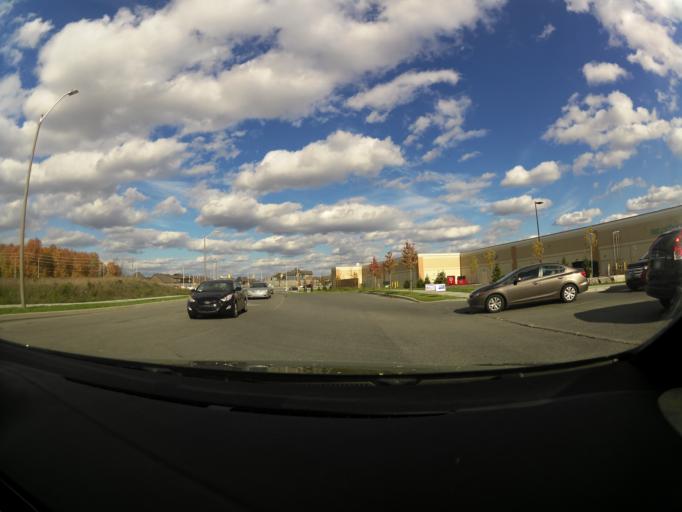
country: CA
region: Ontario
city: Bells Corners
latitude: 45.2706
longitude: -75.7849
